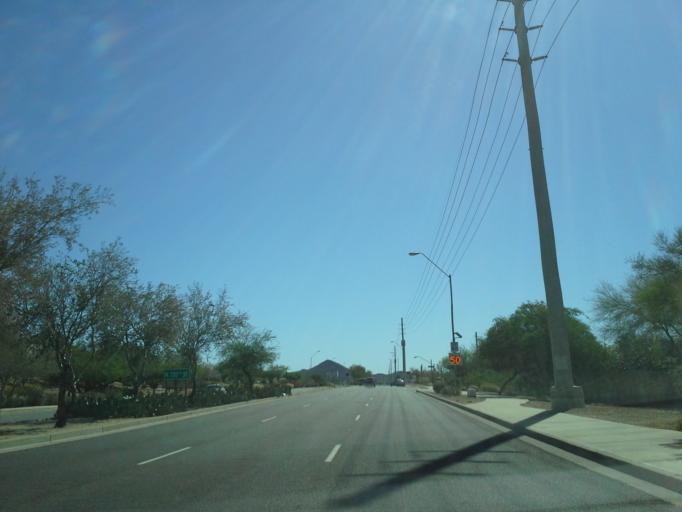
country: US
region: Arizona
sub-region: Maricopa County
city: Scottsdale
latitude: 33.5823
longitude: -111.8236
